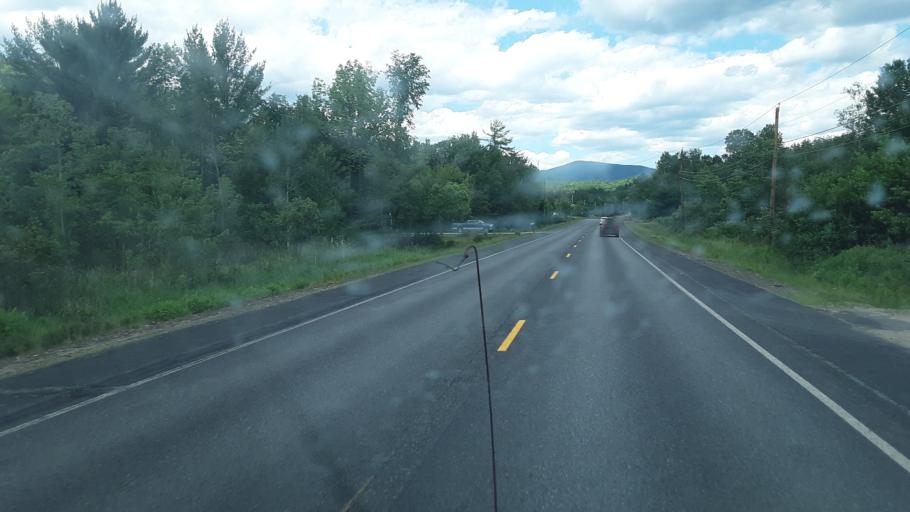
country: US
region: Maine
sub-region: Oxford County
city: Peru
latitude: 44.5657
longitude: -70.3744
